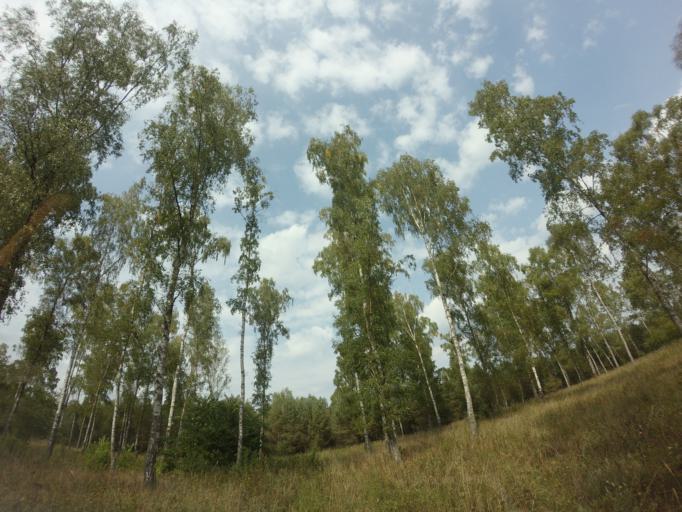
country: PL
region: West Pomeranian Voivodeship
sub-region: Powiat drawski
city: Drawsko Pomorskie
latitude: 53.4605
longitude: 15.7078
